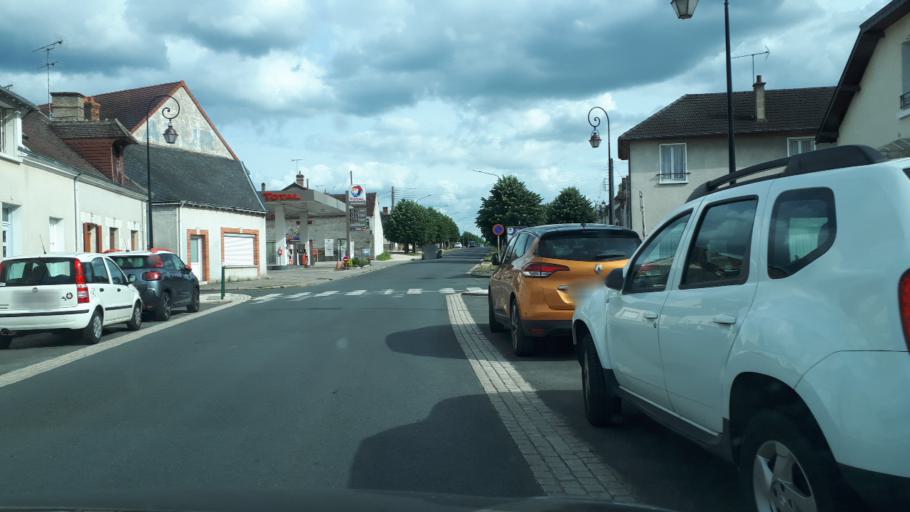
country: FR
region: Centre
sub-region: Departement du Loir-et-Cher
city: Romorantin-Lanthenay
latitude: 47.3536
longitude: 1.7439
